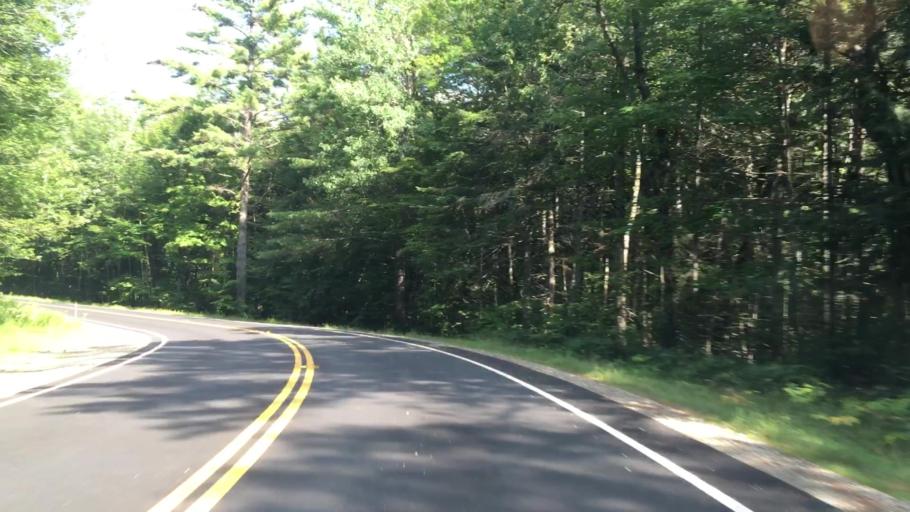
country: US
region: New Hampshire
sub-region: Grafton County
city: North Haverhill
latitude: 44.1004
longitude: -71.8604
